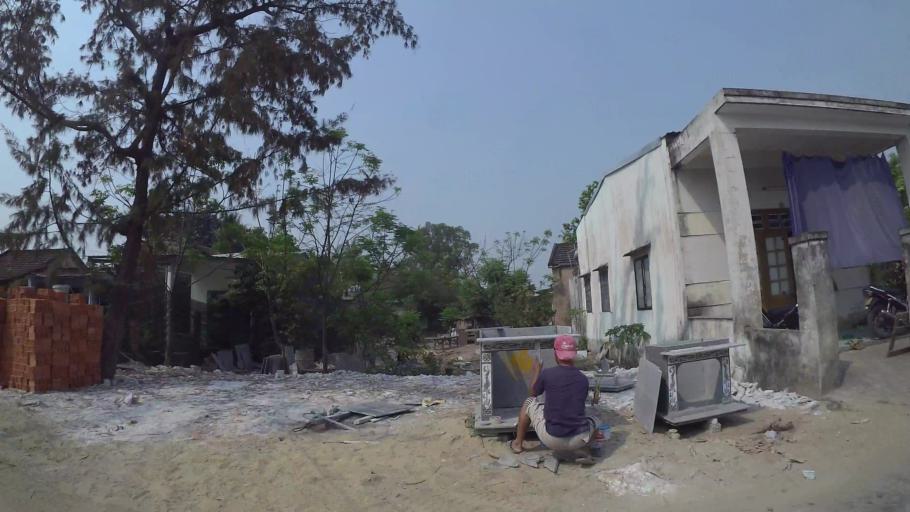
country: VN
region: Da Nang
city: Ngu Hanh Son
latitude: 15.9920
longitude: 108.2396
